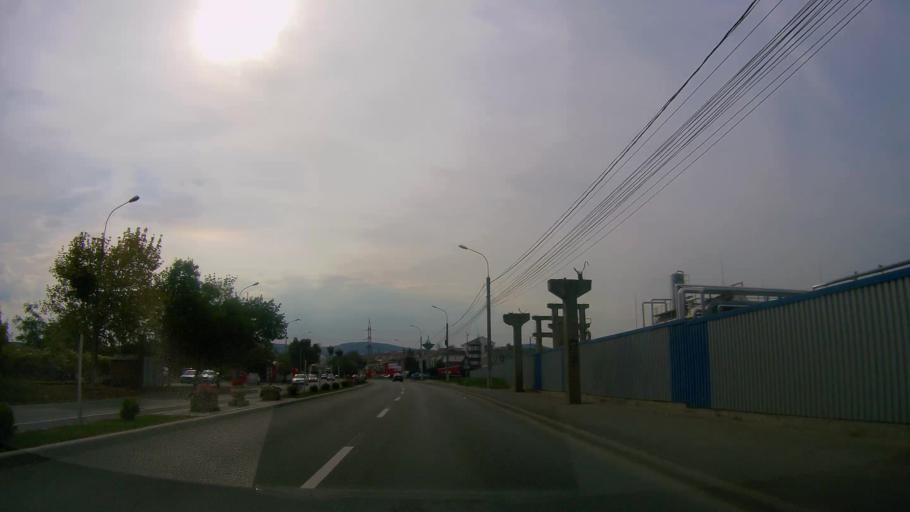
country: RO
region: Salaj
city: Zalau
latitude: 47.2074
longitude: 23.0457
